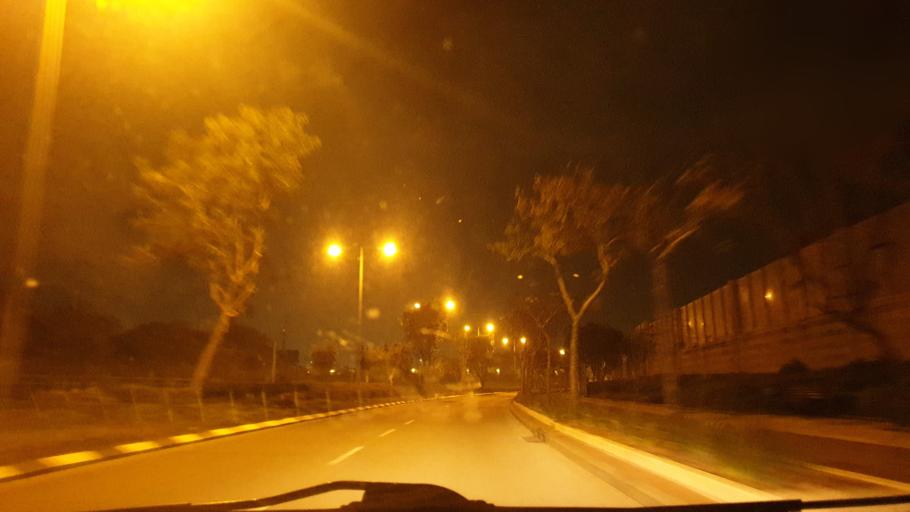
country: IL
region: Central District
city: Bet Dagan
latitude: 31.9707
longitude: 34.8248
